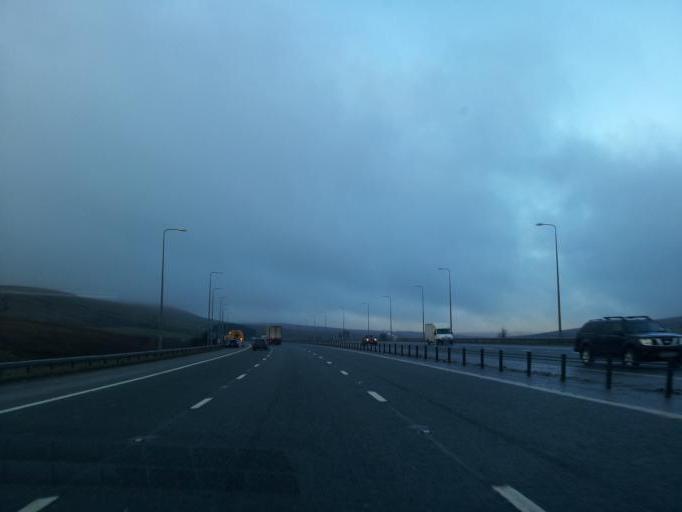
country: GB
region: England
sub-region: Calderdale
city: Ripponden
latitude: 53.6457
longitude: -1.9416
